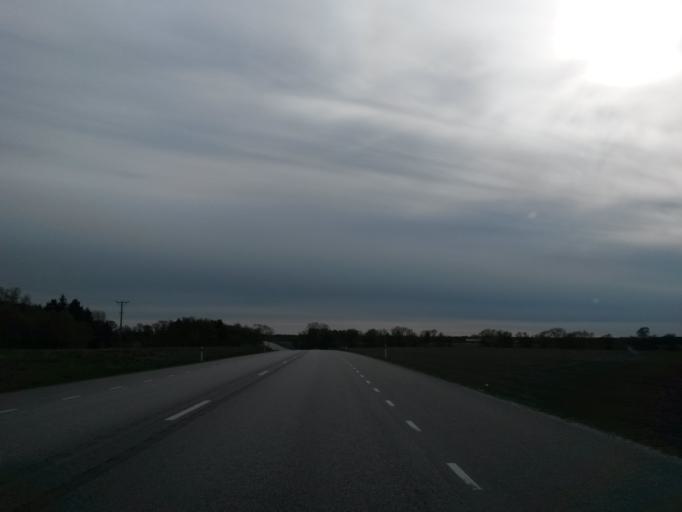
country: SE
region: Vaestra Goetaland
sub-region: Vara Kommun
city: Vara
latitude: 58.2466
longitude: 12.9493
